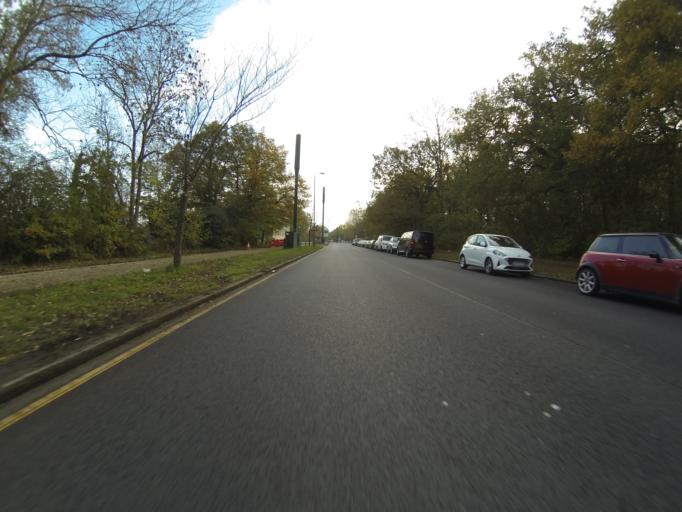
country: GB
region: England
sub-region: Greater London
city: Welling
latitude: 51.4604
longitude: 0.0772
